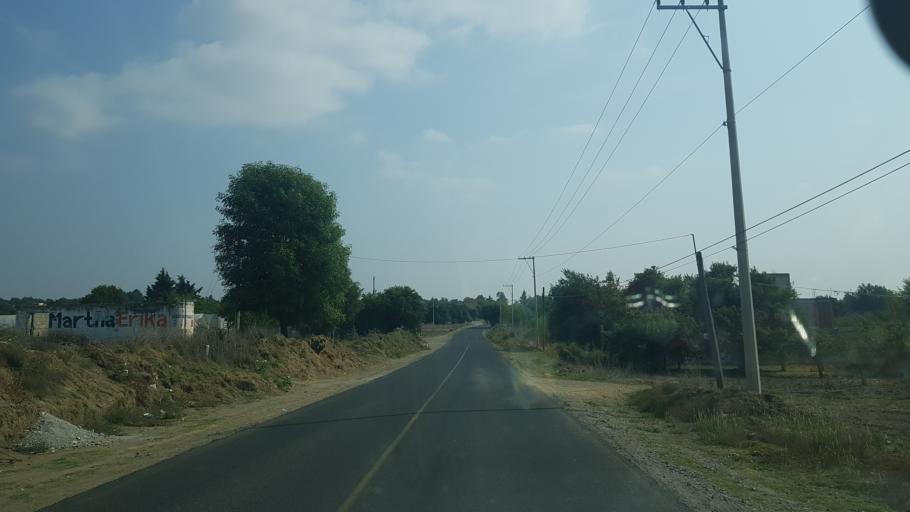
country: MX
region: Puebla
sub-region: Huejotzingo
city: San Juan Pancoac
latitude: 19.1260
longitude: -98.4211
